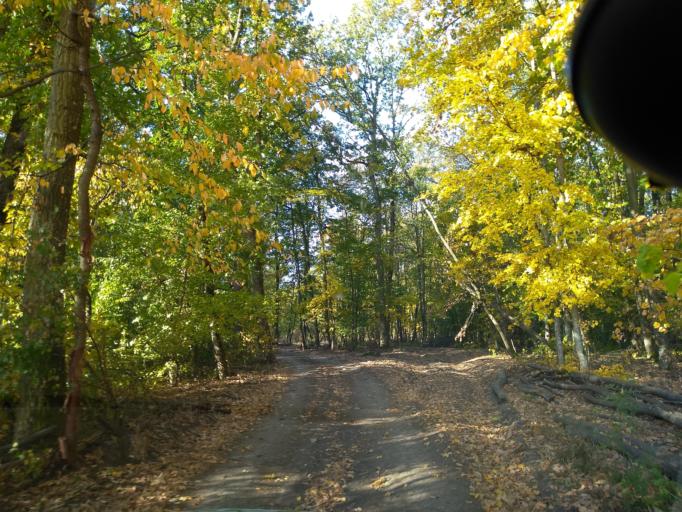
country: RO
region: Timis
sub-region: Comuna Bogda
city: Bogda
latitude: 45.9268
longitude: 21.6238
